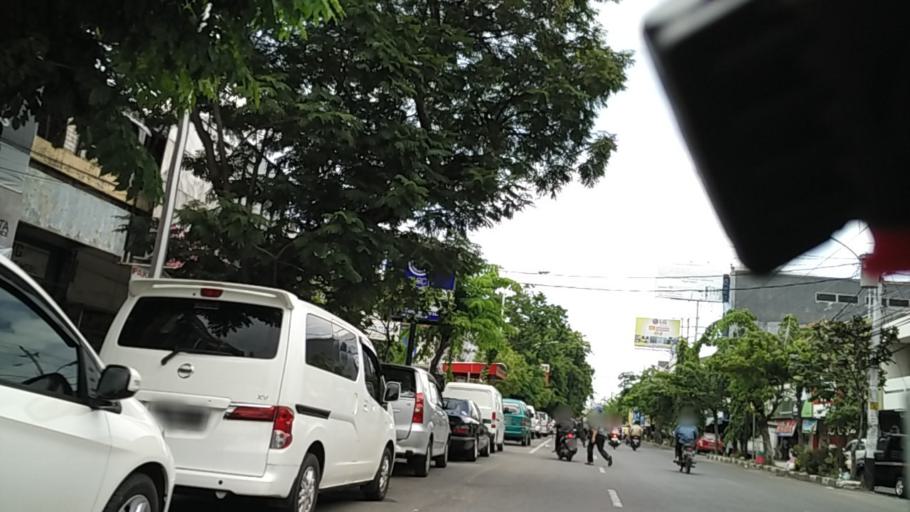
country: ID
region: Central Java
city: Semarang
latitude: -6.9827
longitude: 110.4315
